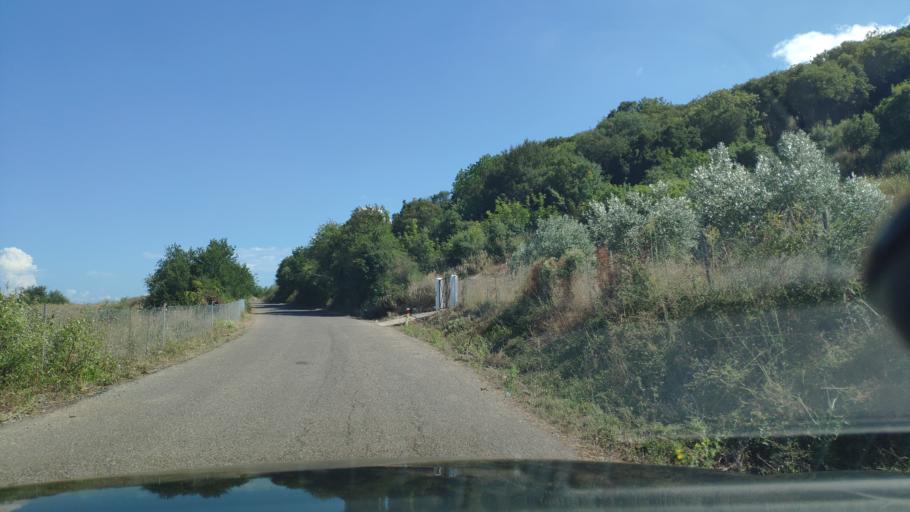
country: GR
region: West Greece
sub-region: Nomos Aitolias kai Akarnanias
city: Katouna
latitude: 38.8018
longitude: 21.1117
